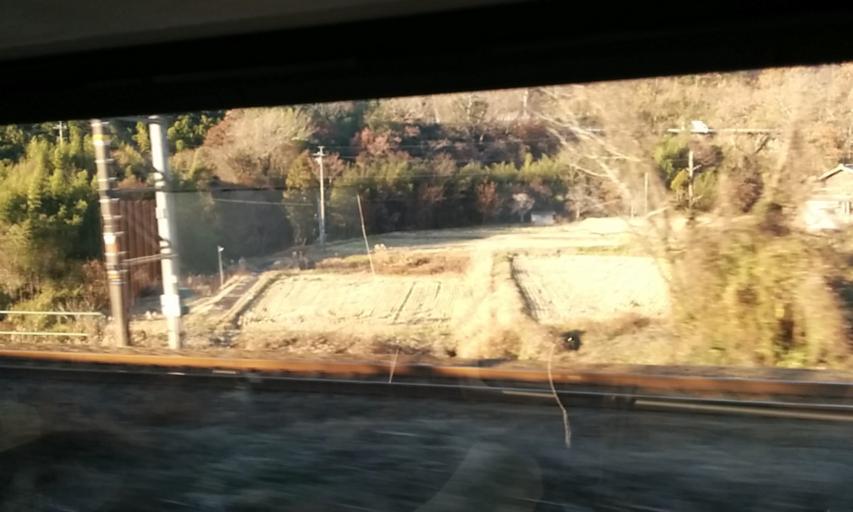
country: JP
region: Gifu
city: Mizunami
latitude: 35.4391
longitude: 137.3579
